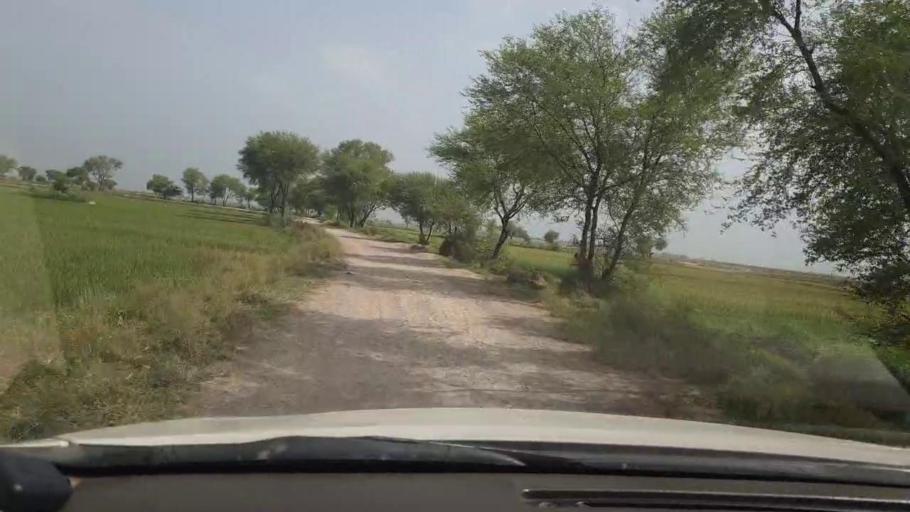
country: PK
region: Sindh
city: Shikarpur
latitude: 28.0183
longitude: 68.5936
